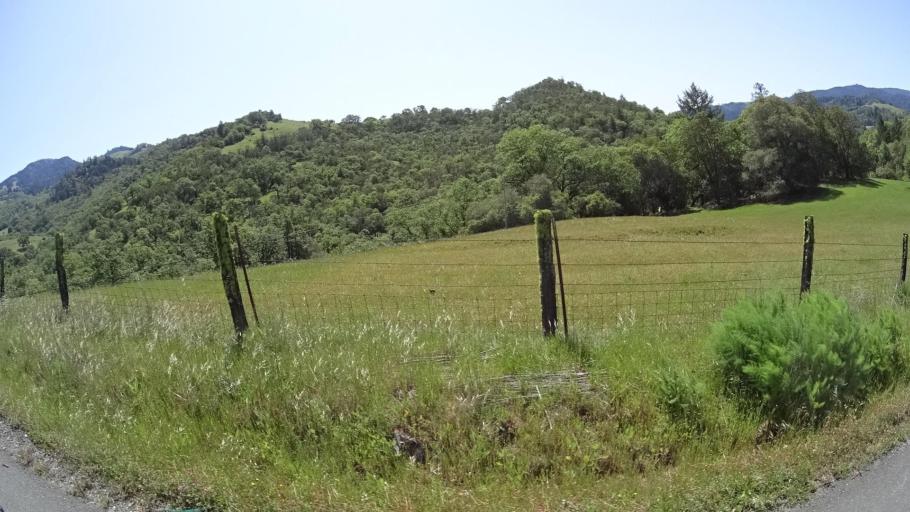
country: US
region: California
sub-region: Humboldt County
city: Redway
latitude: 40.1769
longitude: -123.5972
